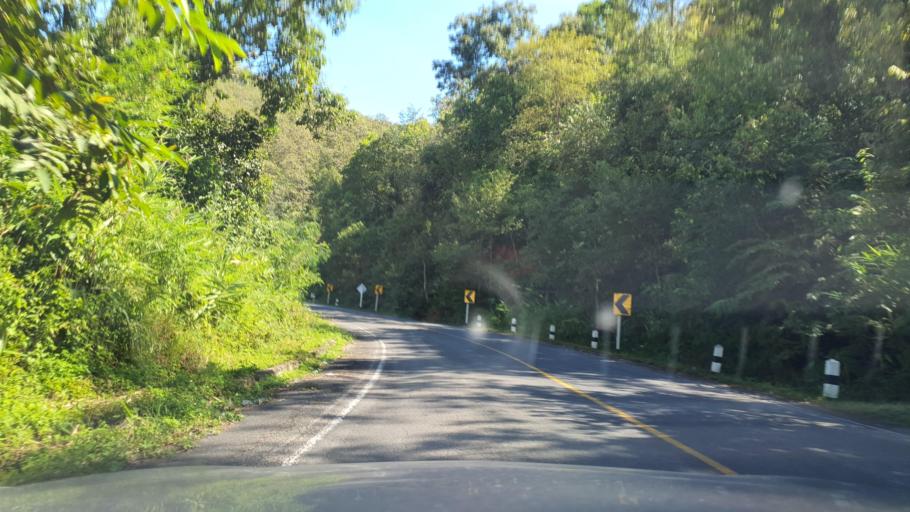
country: TH
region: Chiang Mai
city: Phrao
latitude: 19.3690
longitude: 99.2453
